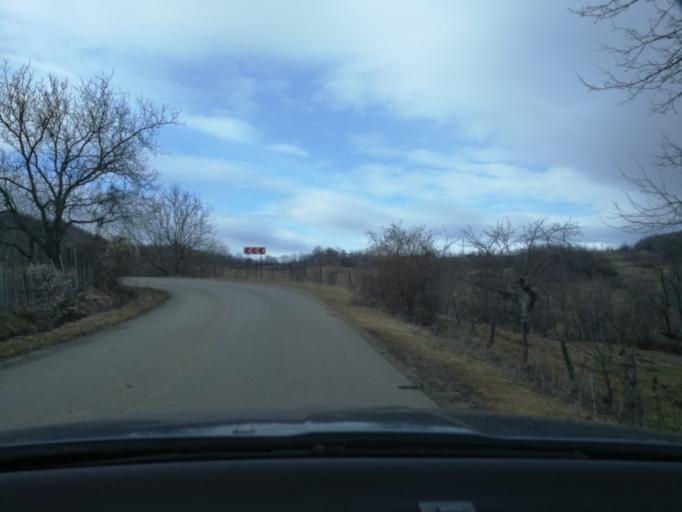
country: RO
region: Dambovita
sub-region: Comuna Buciumeni
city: Buciumeni
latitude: 45.1360
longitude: 25.4631
